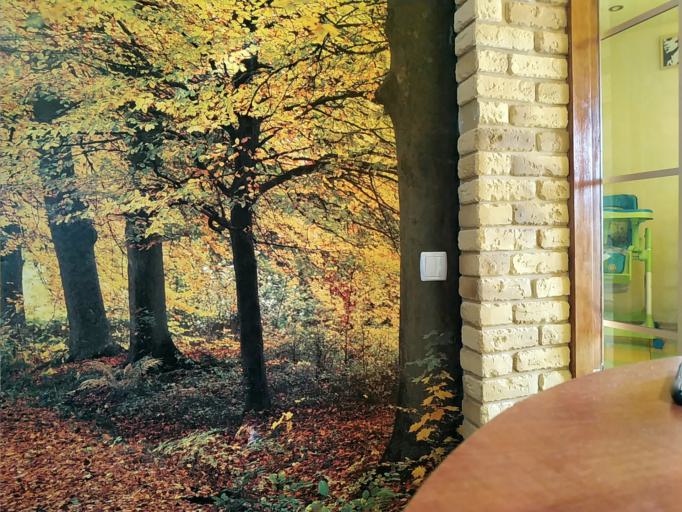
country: RU
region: Novgorod
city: Parfino
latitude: 57.7982
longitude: 31.6210
